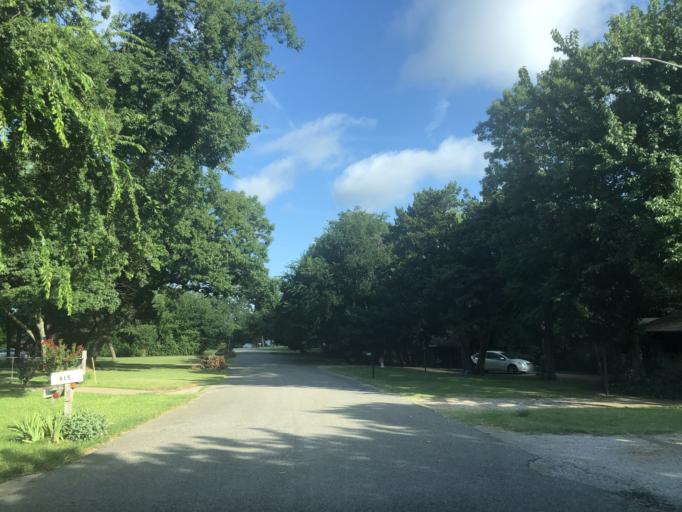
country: US
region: Texas
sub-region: Dallas County
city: Duncanville
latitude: 32.6660
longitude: -96.9198
